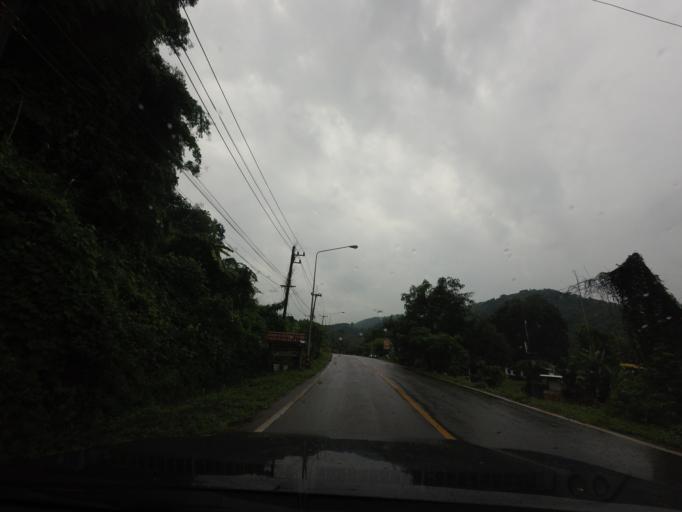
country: TH
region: Nong Khai
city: Sangkhom
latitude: 18.2052
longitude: 102.1207
